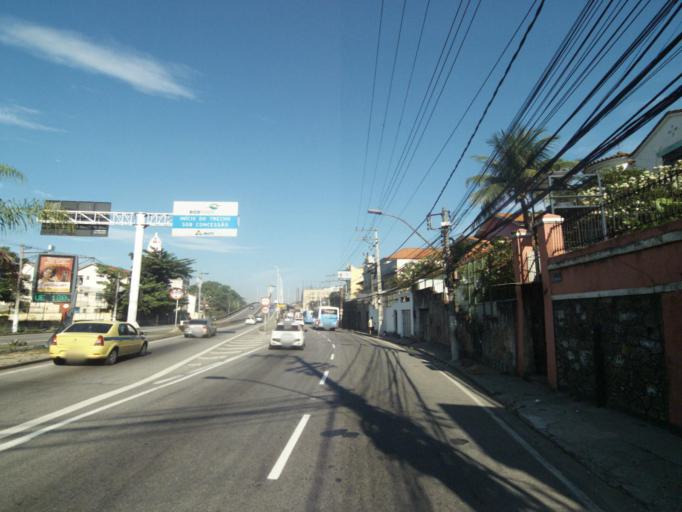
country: BR
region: Rio de Janeiro
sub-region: Niteroi
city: Niteroi
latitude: -22.8805
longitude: -43.1068
